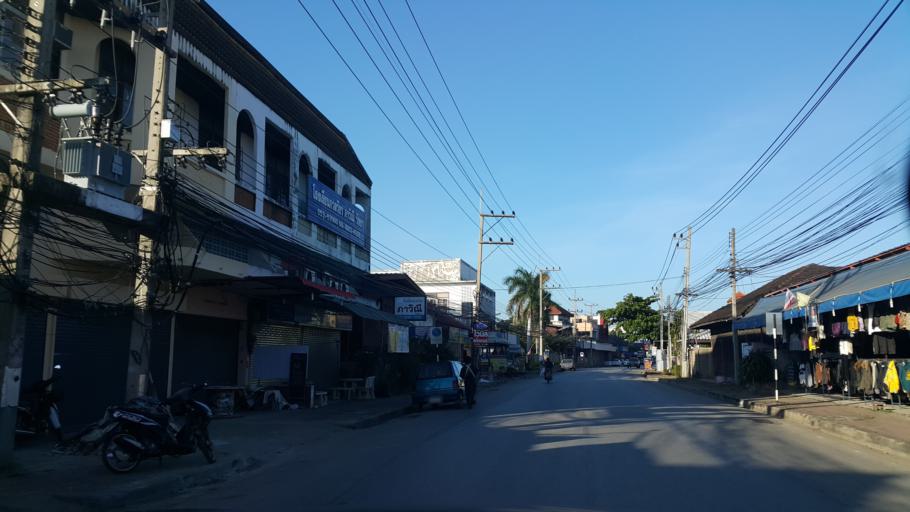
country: TH
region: Lamphun
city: Lamphun
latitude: 18.5958
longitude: 99.0157
